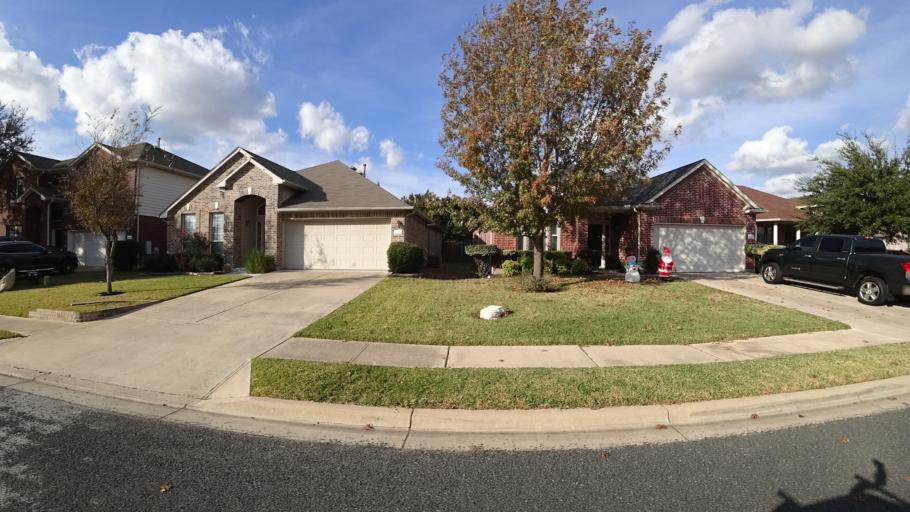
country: US
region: Texas
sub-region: Williamson County
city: Brushy Creek
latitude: 30.5060
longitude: -97.7238
